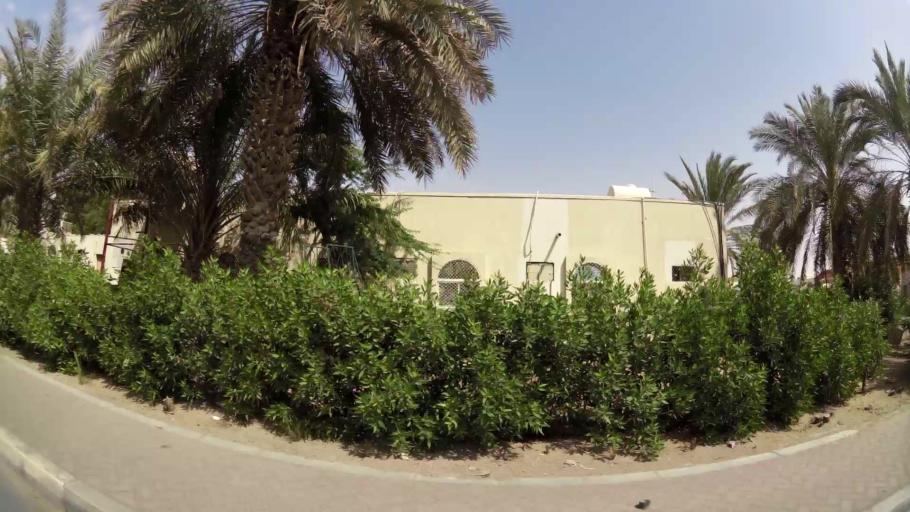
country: AE
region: Abu Dhabi
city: Abu Dhabi
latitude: 24.2944
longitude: 54.6313
